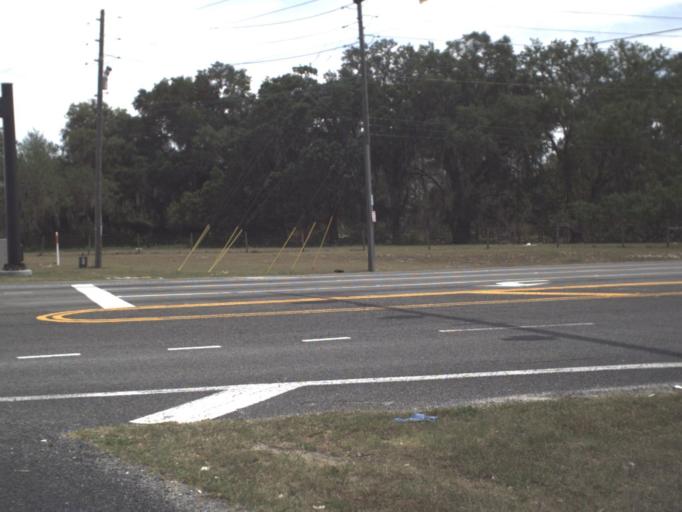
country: US
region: Florida
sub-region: Sumter County
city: Wildwood
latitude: 28.8240
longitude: -81.9746
